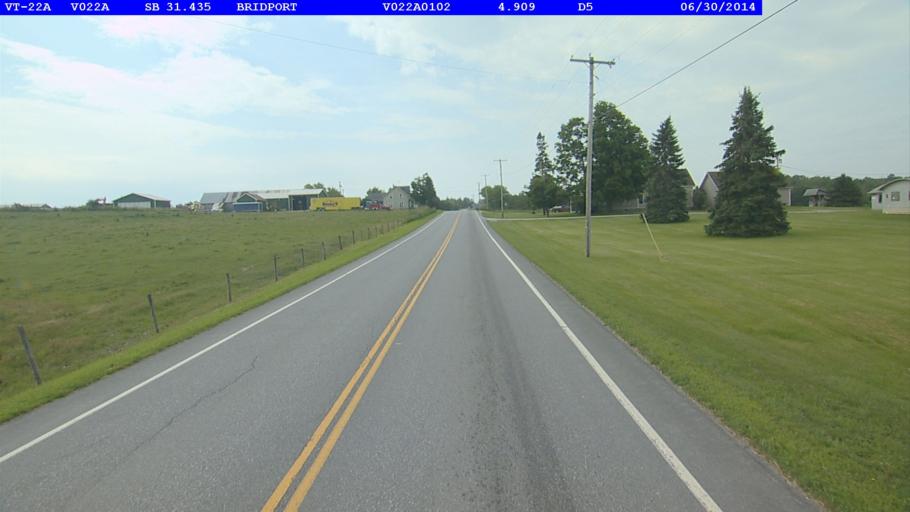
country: US
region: Vermont
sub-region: Addison County
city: Middlebury (village)
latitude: 44.0104
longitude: -73.3094
